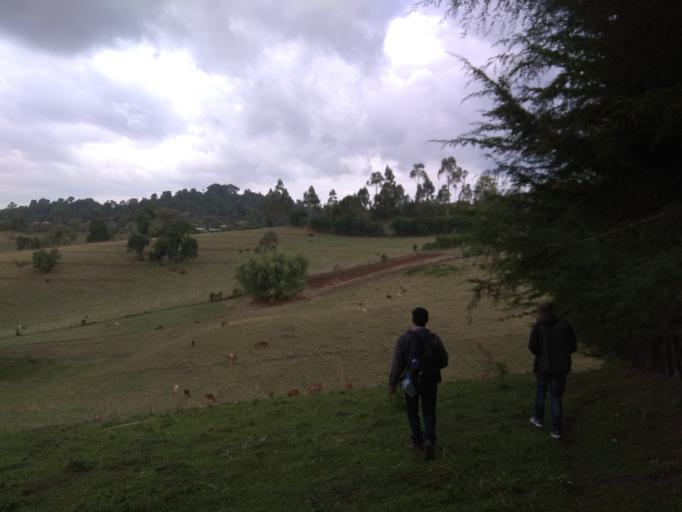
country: ET
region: Oromiya
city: Guder
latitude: 8.7520
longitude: 37.6267
